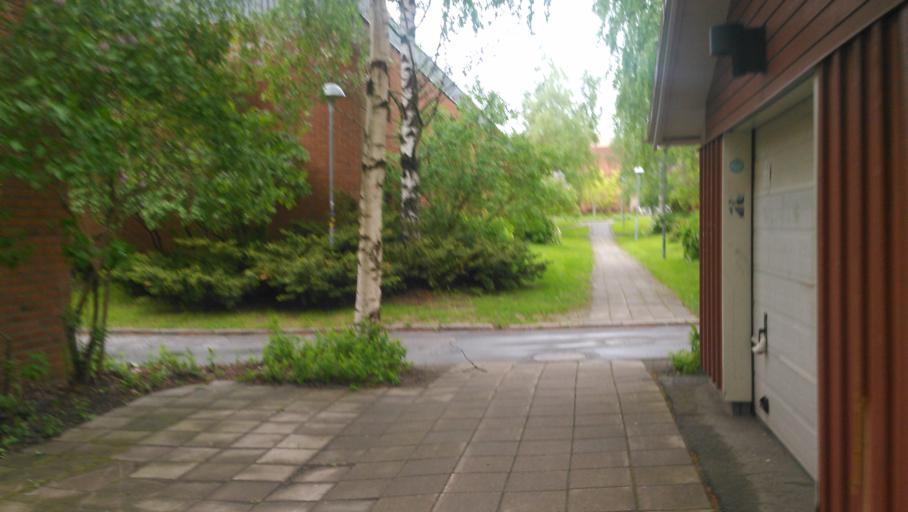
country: SE
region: Vaesterbotten
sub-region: Umea Kommun
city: Umea
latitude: 63.8115
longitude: 20.3092
